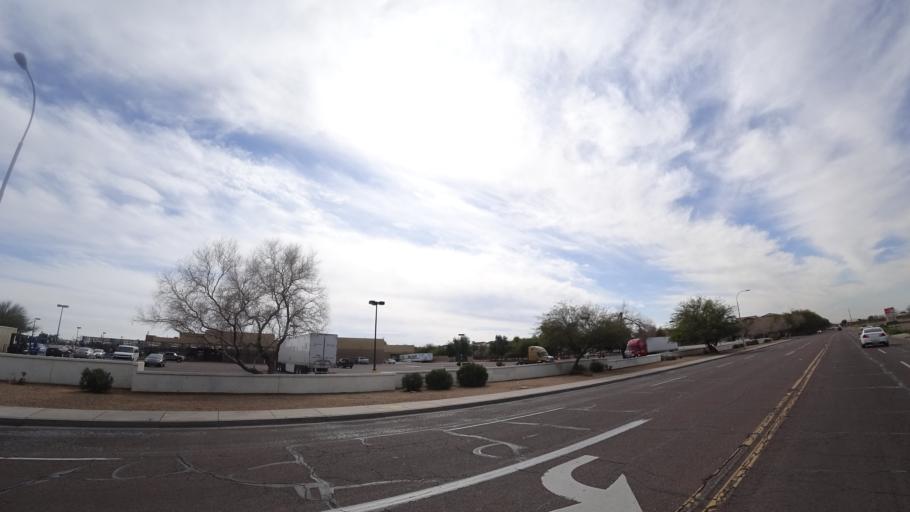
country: US
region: Arizona
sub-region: Maricopa County
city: Tolleson
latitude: 33.4729
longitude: -112.2231
